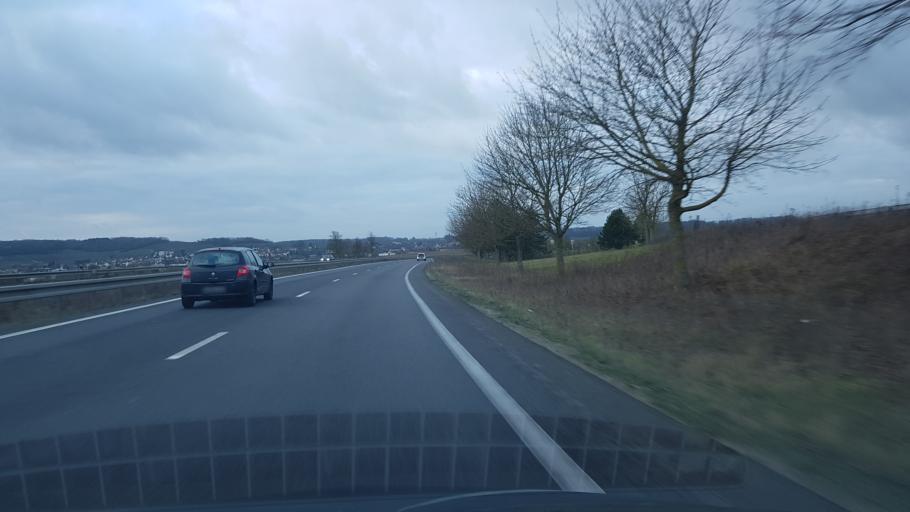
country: FR
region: Champagne-Ardenne
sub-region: Departement de la Marne
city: Sezanne
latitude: 48.7195
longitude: 3.7465
